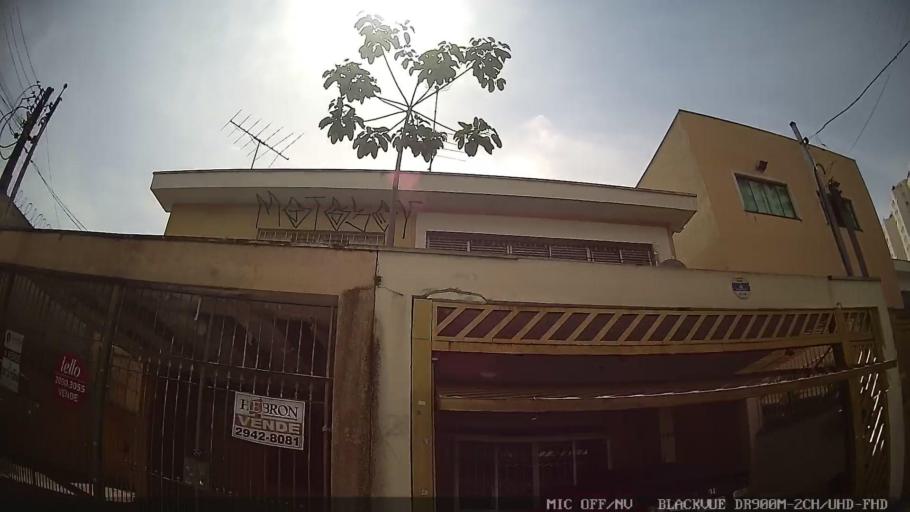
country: BR
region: Sao Paulo
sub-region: Sao Paulo
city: Sao Paulo
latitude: -23.5376
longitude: -46.5729
